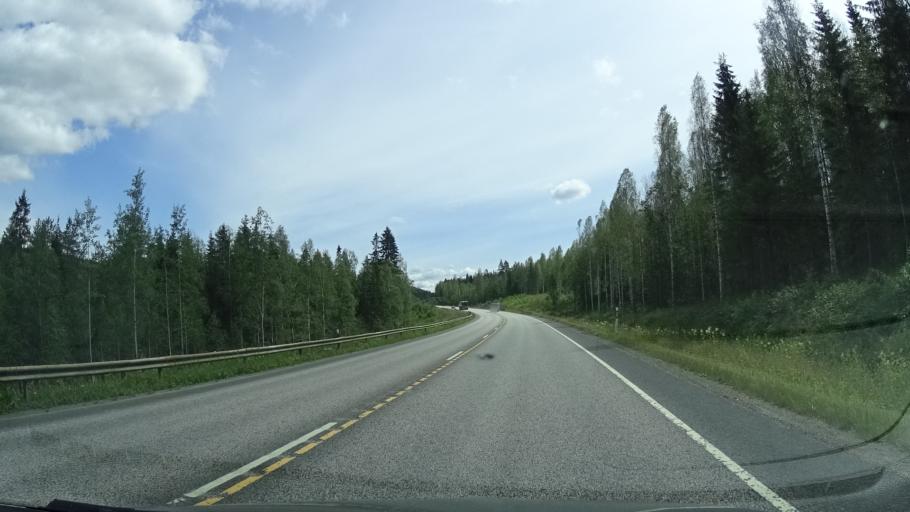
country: FI
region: Central Finland
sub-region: Jyvaeskylae
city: Jyvaeskylae
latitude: 62.2546
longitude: 25.6262
